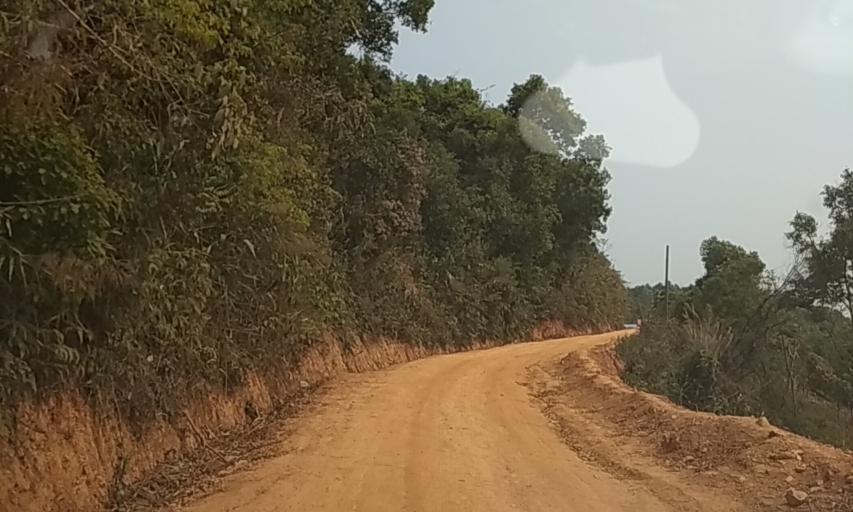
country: TH
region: Nan
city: Chaloem Phra Kiat
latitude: 20.0089
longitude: 101.1268
